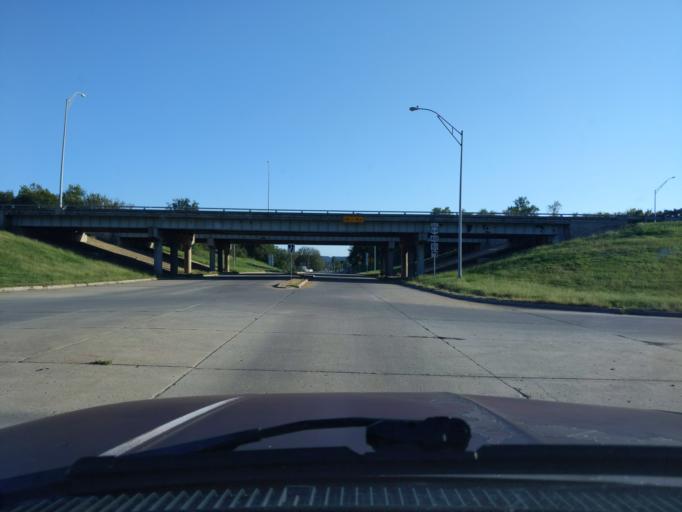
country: US
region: Oklahoma
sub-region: Tulsa County
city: Tulsa
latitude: 36.1593
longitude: -96.0472
